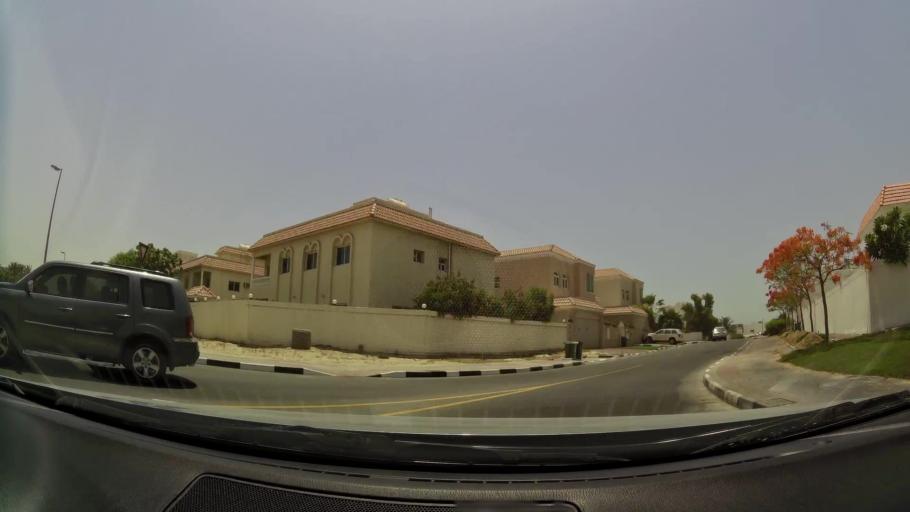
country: AE
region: Dubai
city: Dubai
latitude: 25.1577
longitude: 55.2098
